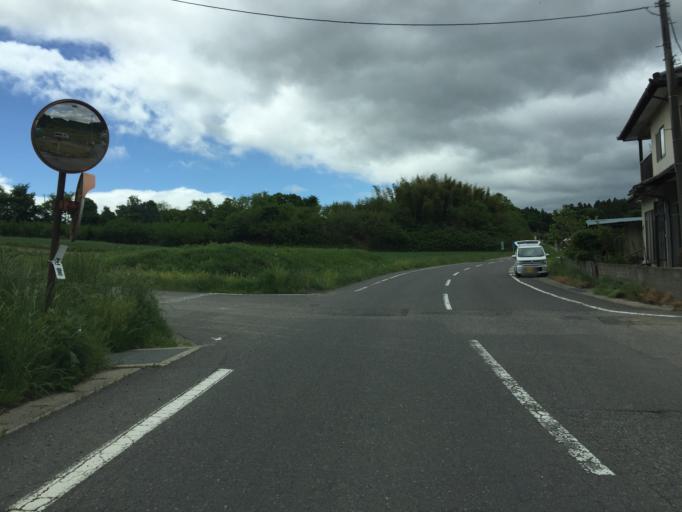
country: JP
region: Fukushima
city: Motomiya
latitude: 37.5111
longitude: 140.4748
